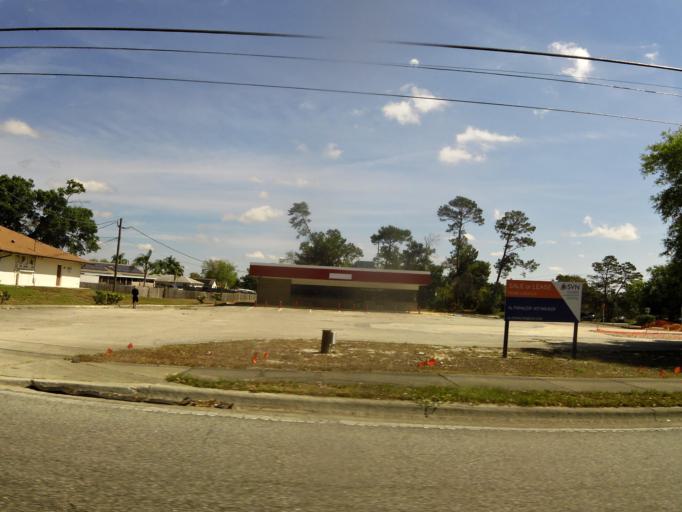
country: US
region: Florida
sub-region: Volusia County
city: Lake Helen
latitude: 28.9447
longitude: -81.2266
